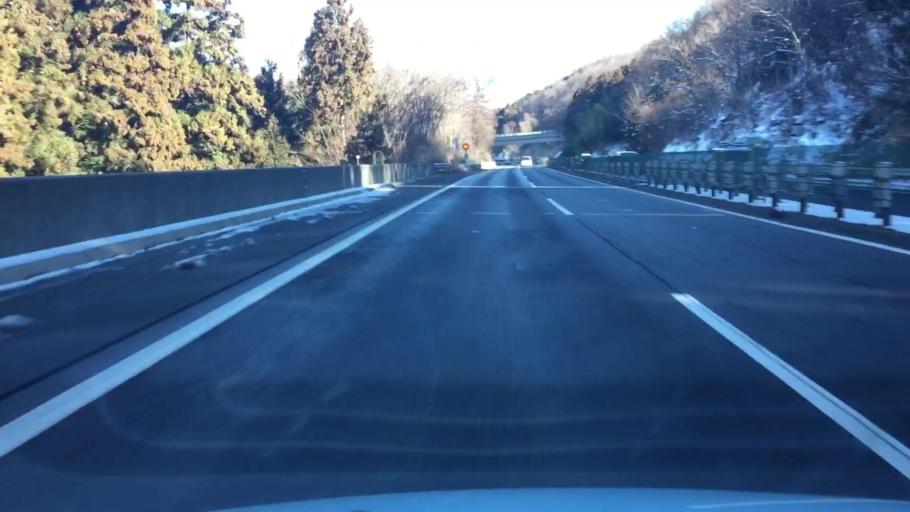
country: JP
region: Gunma
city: Numata
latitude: 36.6346
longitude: 139.0730
